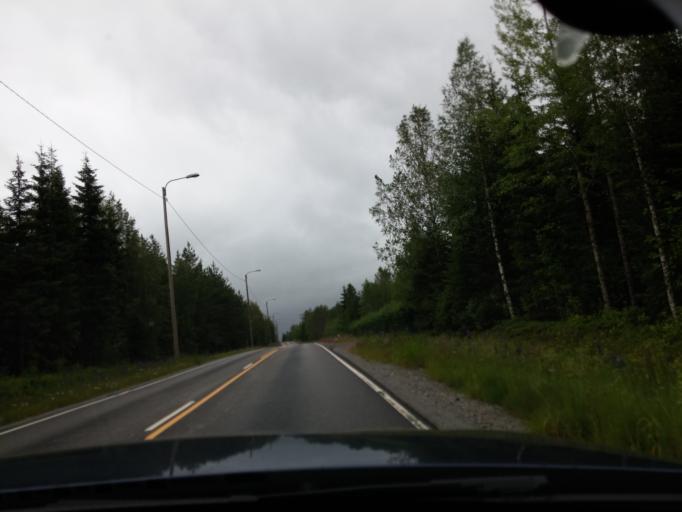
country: FI
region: Central Finland
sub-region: Saarijaervi-Viitasaari
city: Pylkoenmaeki
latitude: 62.6450
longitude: 24.9198
